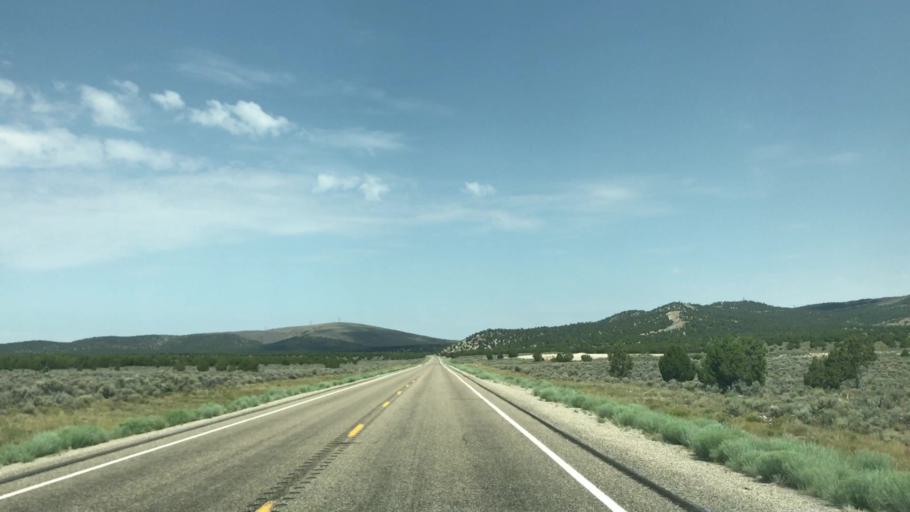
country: US
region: Nevada
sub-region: White Pine County
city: Ely
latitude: 39.3715
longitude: -115.0579
